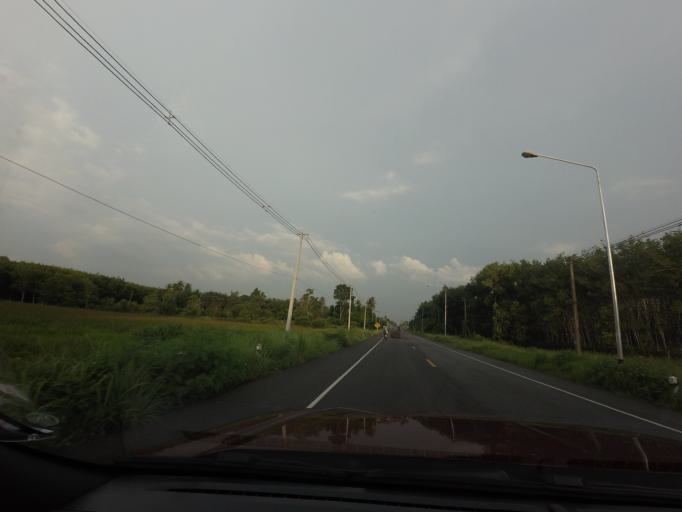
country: TH
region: Pattani
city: Mae Lan
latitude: 6.6552
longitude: 101.1733
